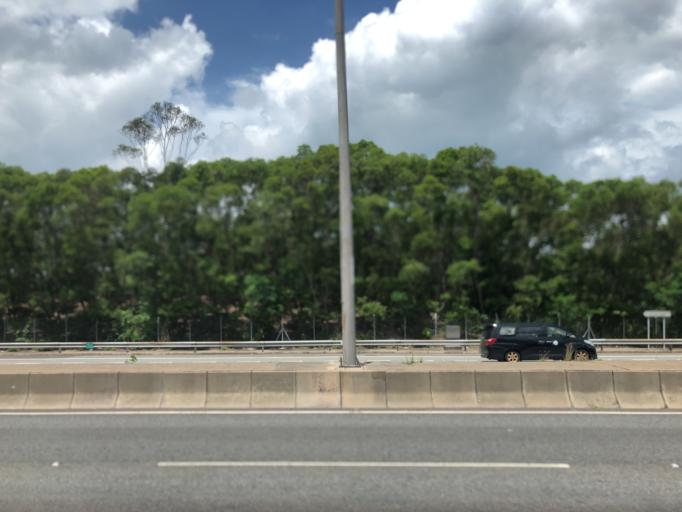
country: HK
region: Tsuen Wan
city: Tsuen Wan
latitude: 22.3591
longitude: 114.0825
